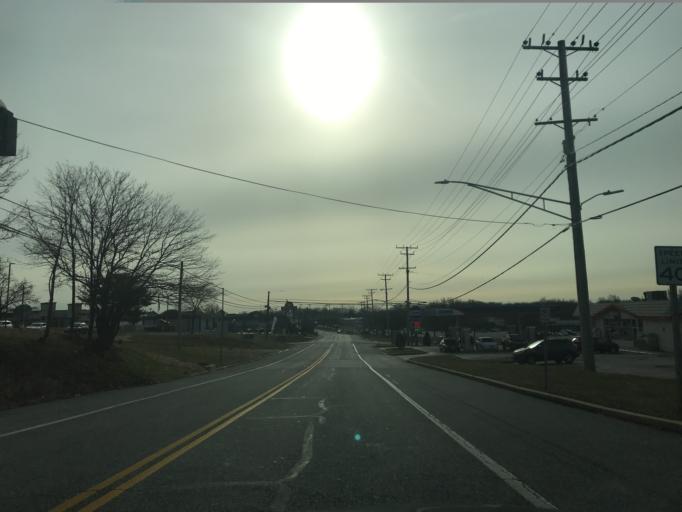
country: US
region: Maryland
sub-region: Harford County
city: Aberdeen
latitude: 39.5235
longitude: -76.1891
